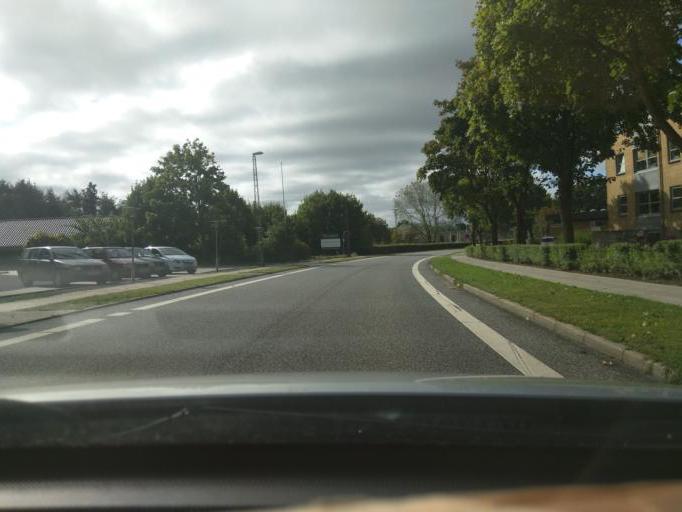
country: DK
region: Central Jutland
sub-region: Viborg Kommune
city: Viborg
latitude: 56.4618
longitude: 9.3951
